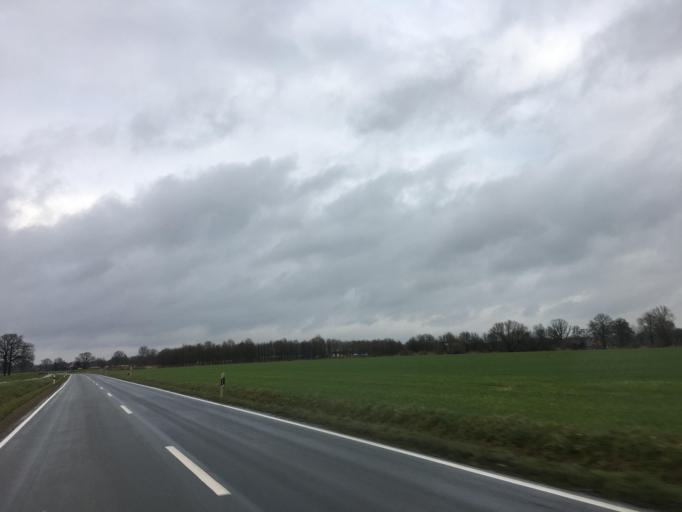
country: DE
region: North Rhine-Westphalia
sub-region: Regierungsbezirk Munster
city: Nordwalde
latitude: 52.1012
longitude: 7.4759
